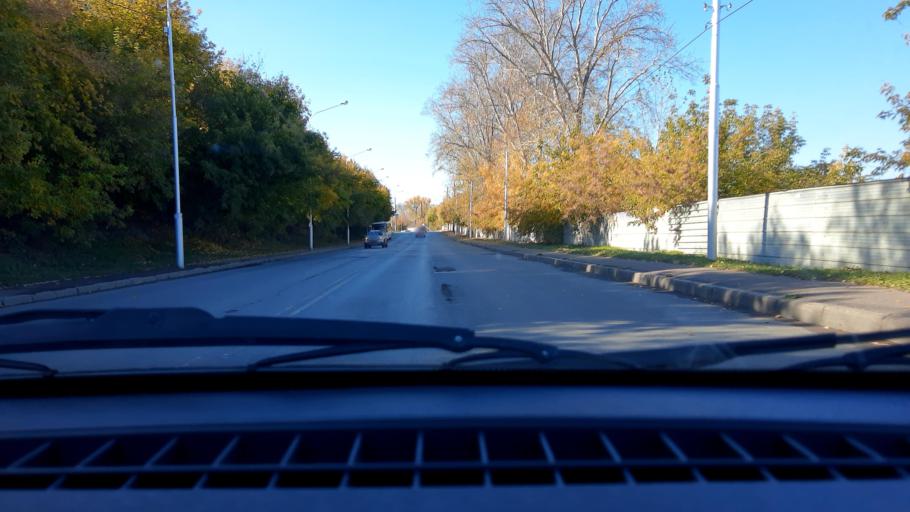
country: RU
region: Bashkortostan
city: Ufa
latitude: 54.7446
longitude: 55.9390
